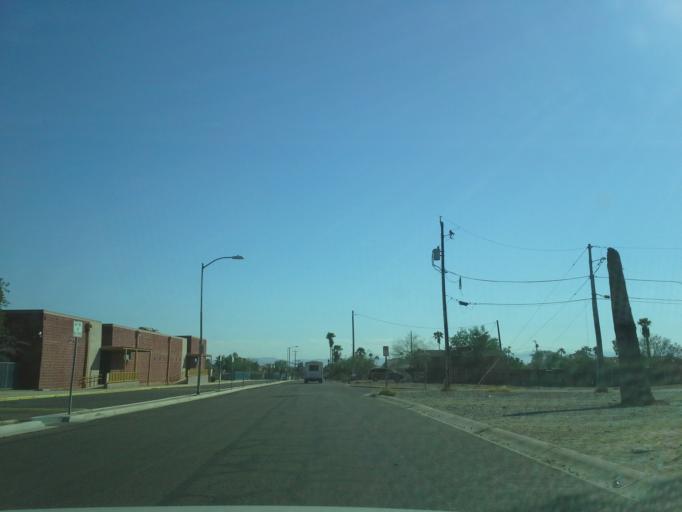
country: US
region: Arizona
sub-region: Maricopa County
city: Glendale
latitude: 33.5809
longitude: -112.0848
